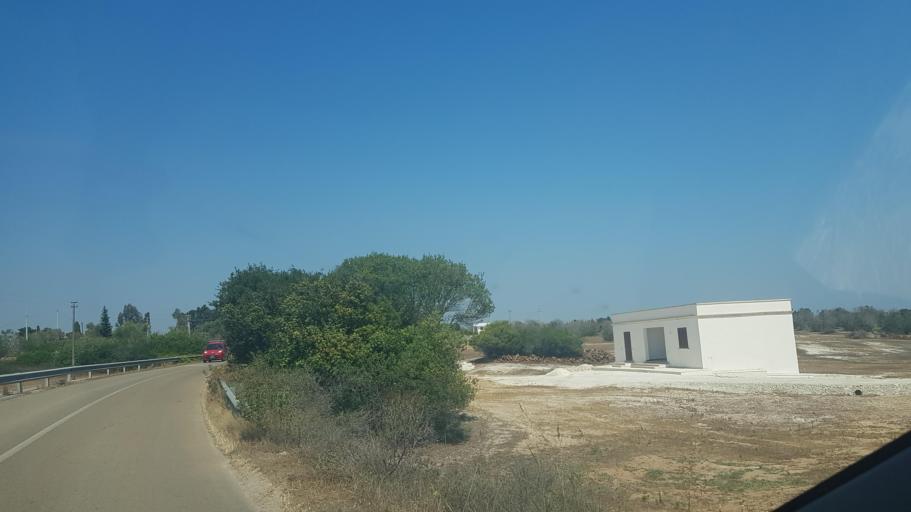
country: IT
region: Apulia
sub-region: Provincia di Lecce
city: Otranto
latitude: 40.1919
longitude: 18.4424
